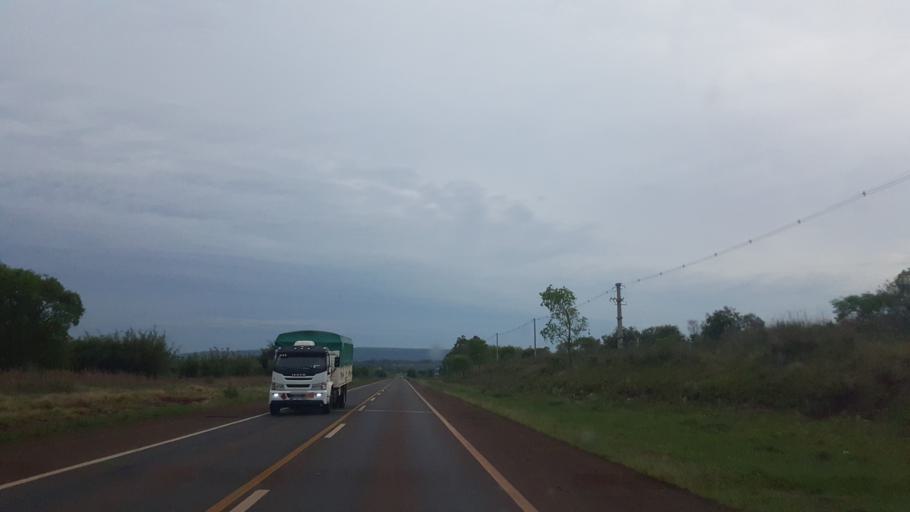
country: AR
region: Misiones
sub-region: Departamento de Apostoles
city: San Jose
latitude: -27.7778
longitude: -55.8108
